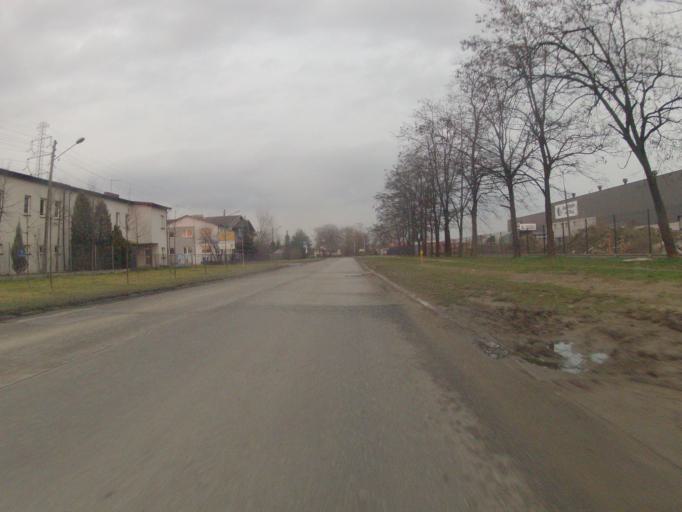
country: PL
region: Lesser Poland Voivodeship
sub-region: Powiat wielicki
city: Czarnochowice
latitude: 50.0504
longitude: 20.0117
